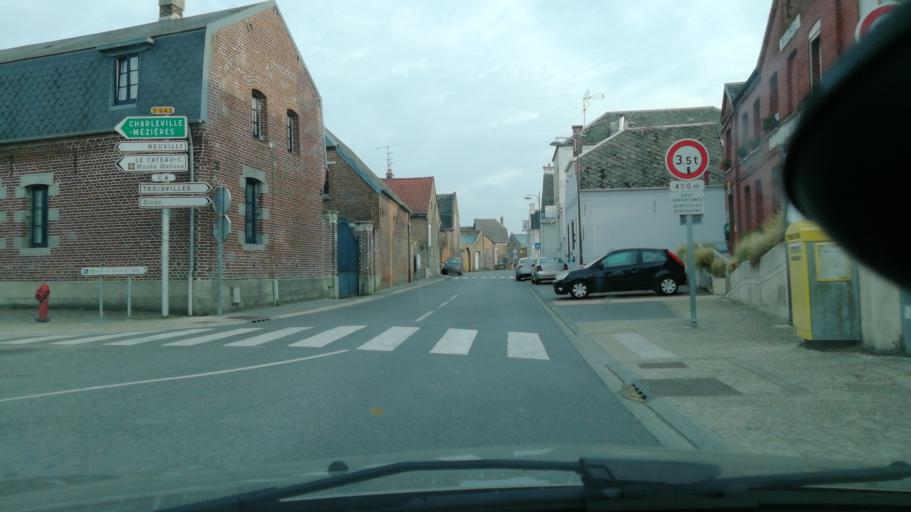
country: FR
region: Nord-Pas-de-Calais
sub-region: Departement du Nord
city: Viesly
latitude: 50.1216
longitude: 3.4639
